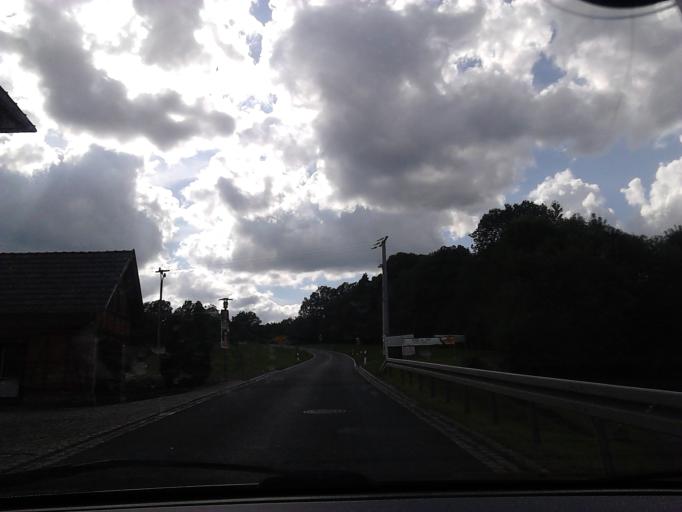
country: DE
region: Bavaria
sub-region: Upper Franconia
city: Weitramsdorf
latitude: 50.2747
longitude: 10.7982
